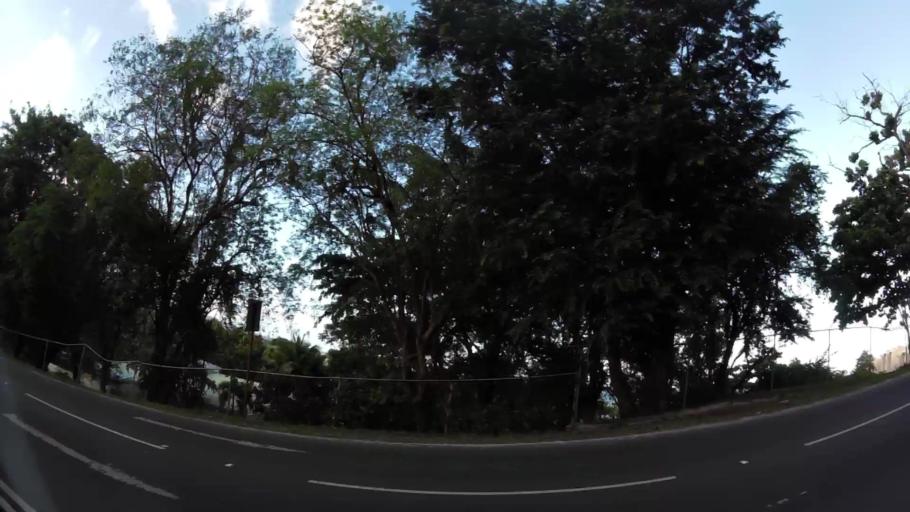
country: LC
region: Castries Quarter
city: Bisee
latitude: 14.0406
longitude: -60.9696
